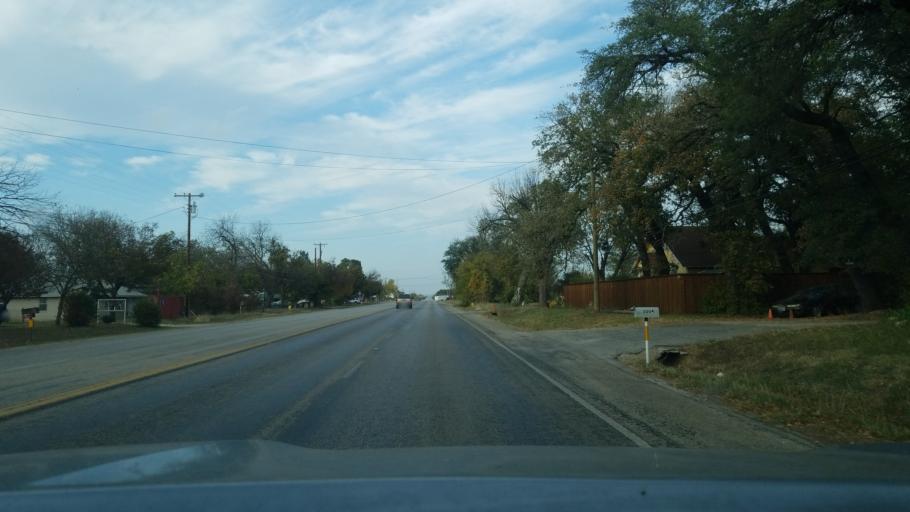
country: US
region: Texas
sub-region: Brown County
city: Early
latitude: 31.7501
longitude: -98.9628
